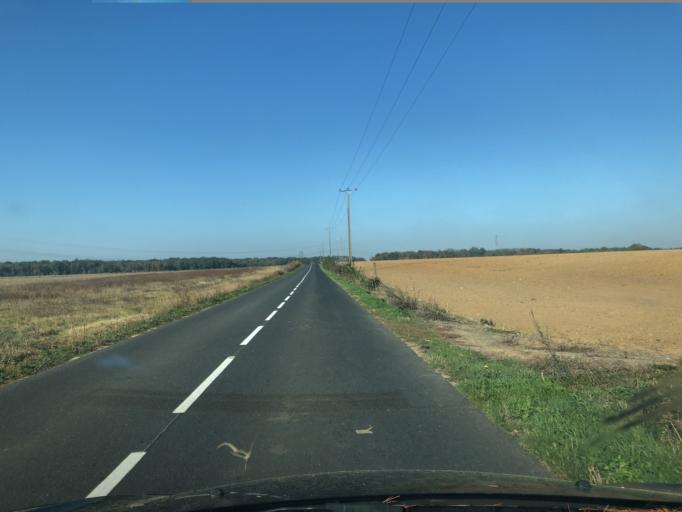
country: FR
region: Centre
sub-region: Departement d'Indre-et-Loire
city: Rouziers-de-Touraine
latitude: 47.5250
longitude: 0.6436
